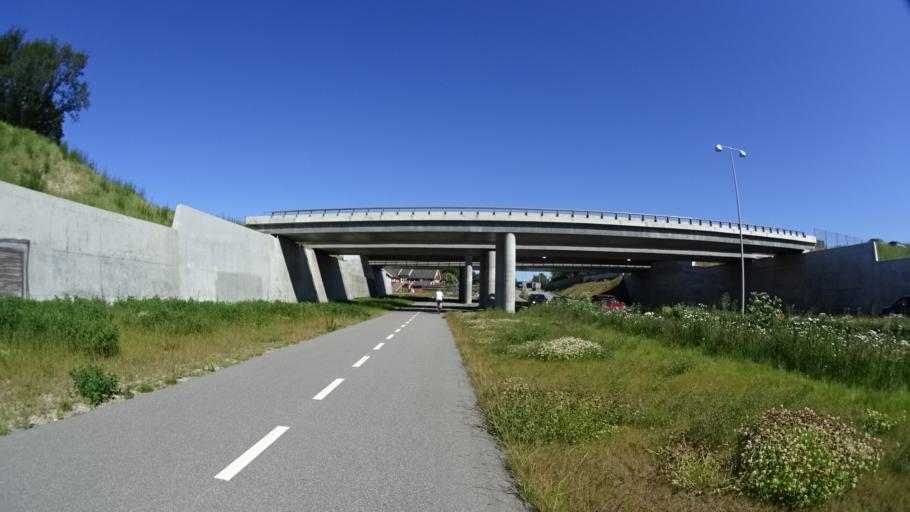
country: DK
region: Central Jutland
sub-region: Arhus Kommune
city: Arhus
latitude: 56.1402
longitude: 10.1733
